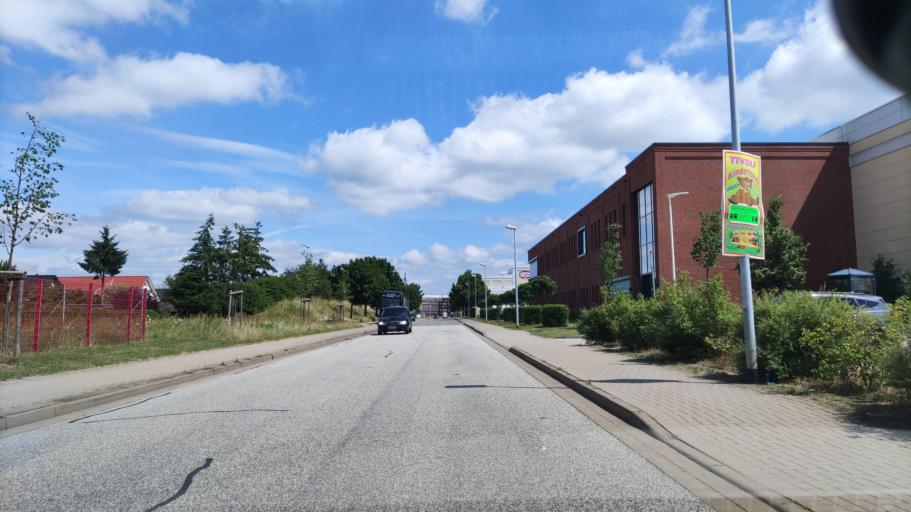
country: DE
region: Mecklenburg-Vorpommern
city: Wittenburg
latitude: 53.4997
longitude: 11.0812
